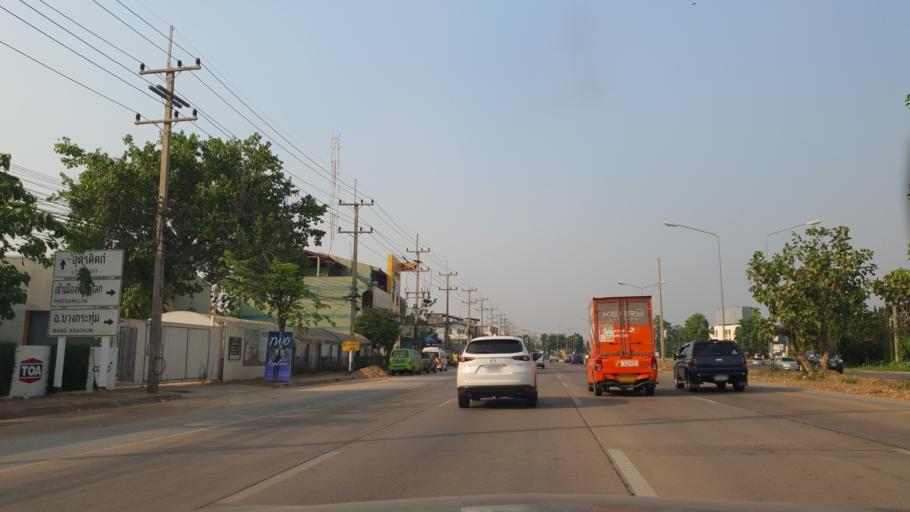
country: TH
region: Phitsanulok
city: Phitsanulok
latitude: 16.7997
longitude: 100.2139
